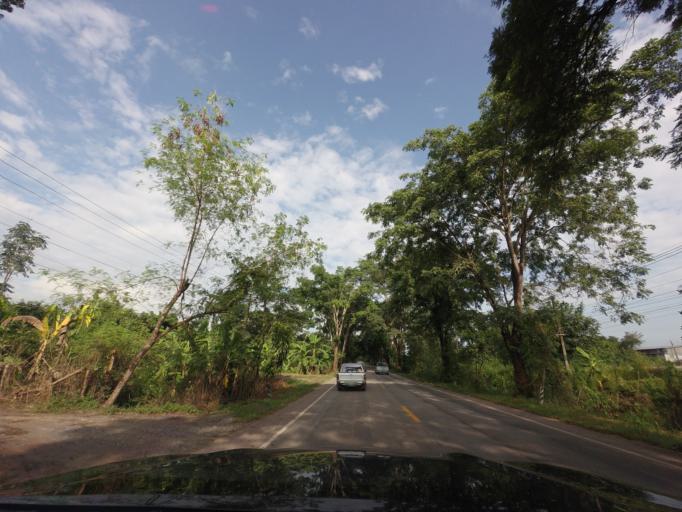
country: TH
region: Nong Khai
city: Pho Tak
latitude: 17.7865
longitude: 102.3682
